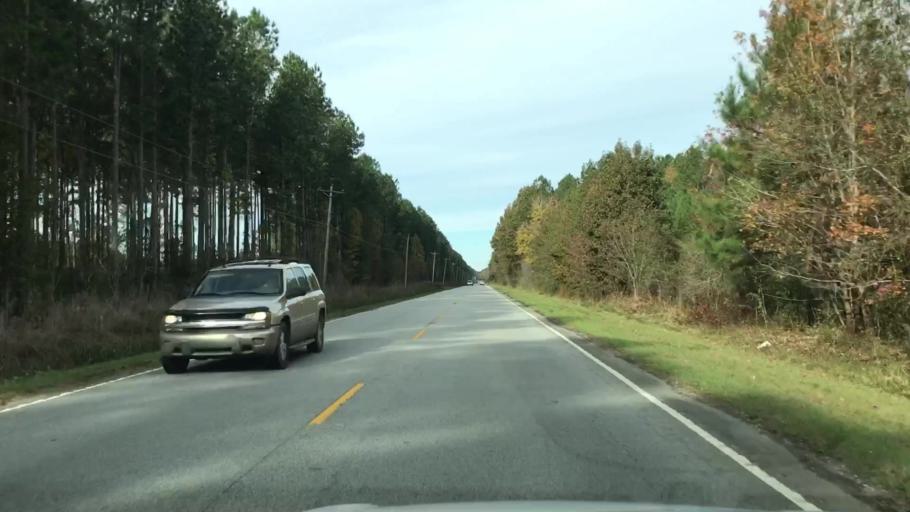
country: US
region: South Carolina
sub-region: Colleton County
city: Walterboro
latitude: 32.8142
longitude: -80.5352
